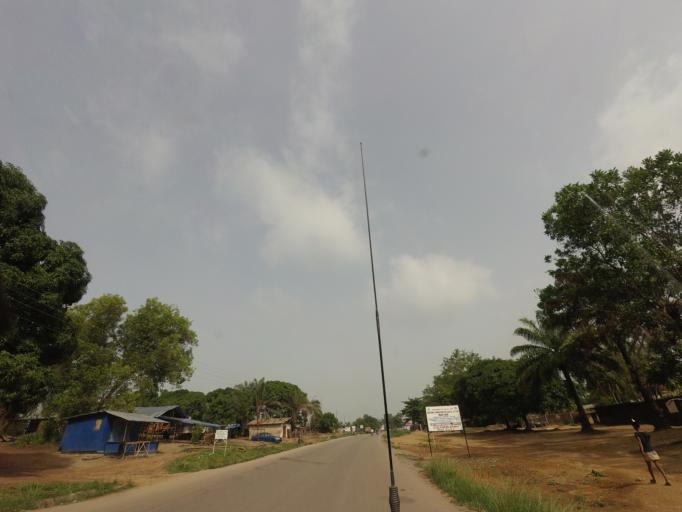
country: SL
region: Southern Province
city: Bo
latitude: 7.9441
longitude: -11.7321
